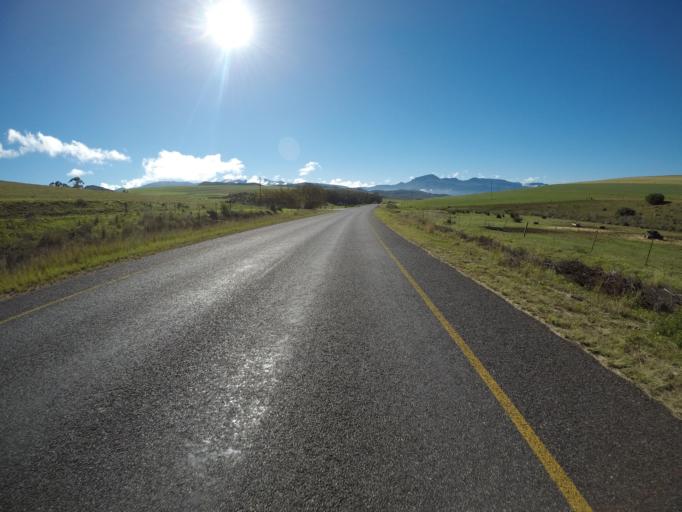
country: ZA
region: Western Cape
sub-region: Overberg District Municipality
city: Caledon
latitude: -34.1262
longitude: 19.5140
